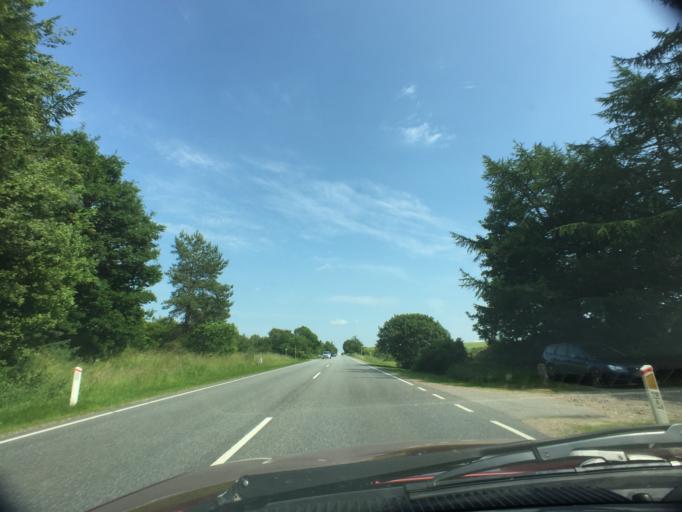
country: DK
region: Central Jutland
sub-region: Favrskov Kommune
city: Hammel
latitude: 56.2440
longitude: 9.7872
